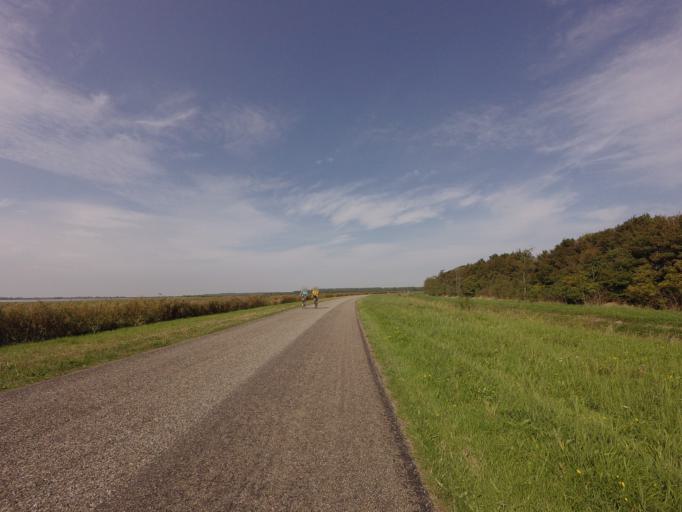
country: NL
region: Groningen
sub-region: Gemeente De Marne
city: Ulrum
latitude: 53.3577
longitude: 6.2620
